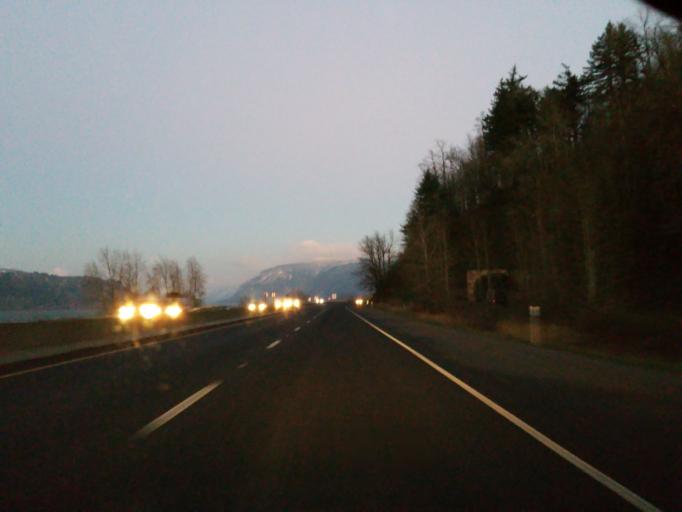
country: US
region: Washington
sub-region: Clark County
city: Washougal
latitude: 45.5418
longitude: -122.2787
